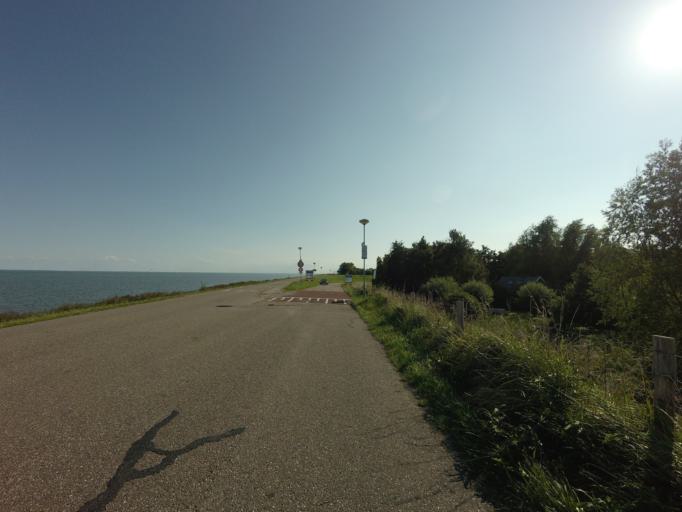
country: NL
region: North Holland
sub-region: Gemeente Enkhuizen
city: Enkhuizen
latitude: 52.6797
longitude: 5.2434
